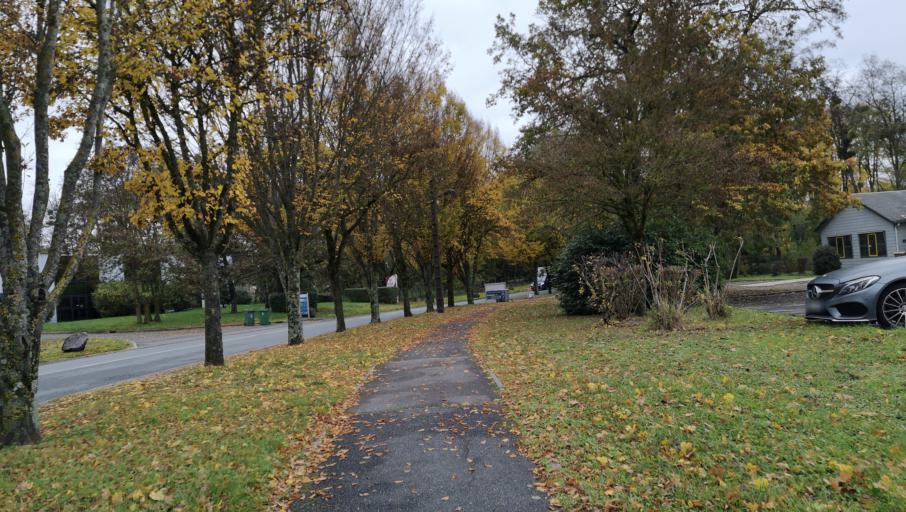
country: FR
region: Centre
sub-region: Departement du Loiret
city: Semoy
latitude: 47.9170
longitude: 1.9512
